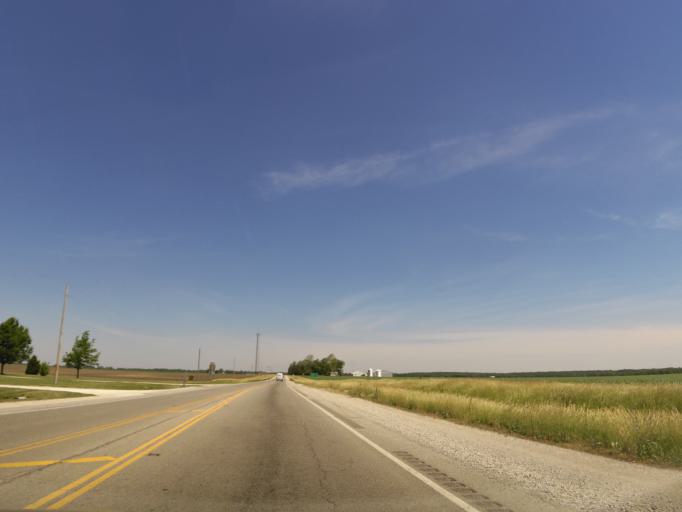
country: US
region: Illinois
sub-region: Vermilion County
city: Rossville
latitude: 40.3007
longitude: -87.6581
